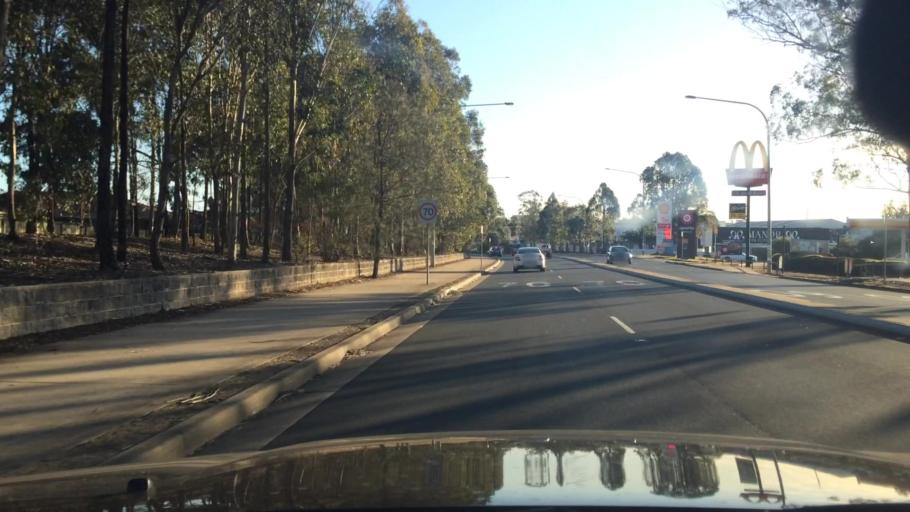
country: AU
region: New South Wales
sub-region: Fairfield
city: Fairfield Heights
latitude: -33.8500
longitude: 150.9022
